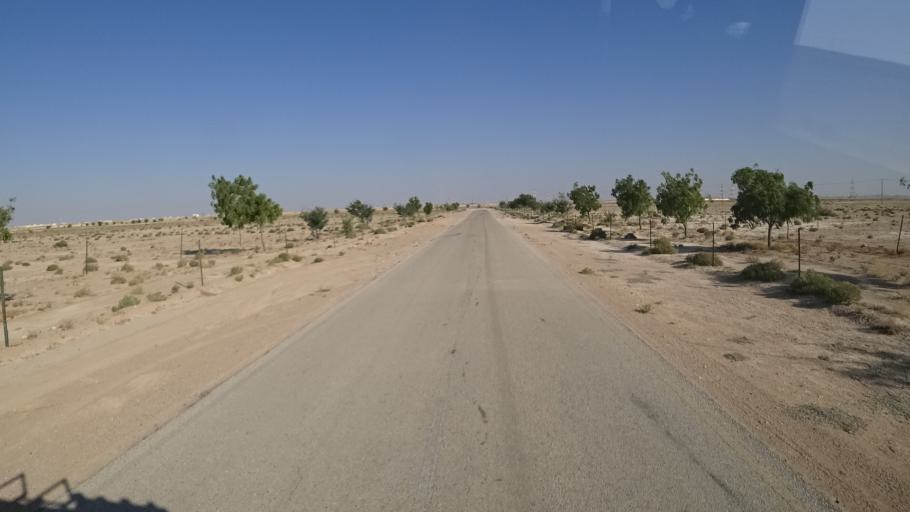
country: OM
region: Zufar
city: Salalah
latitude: 17.5952
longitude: 54.0292
